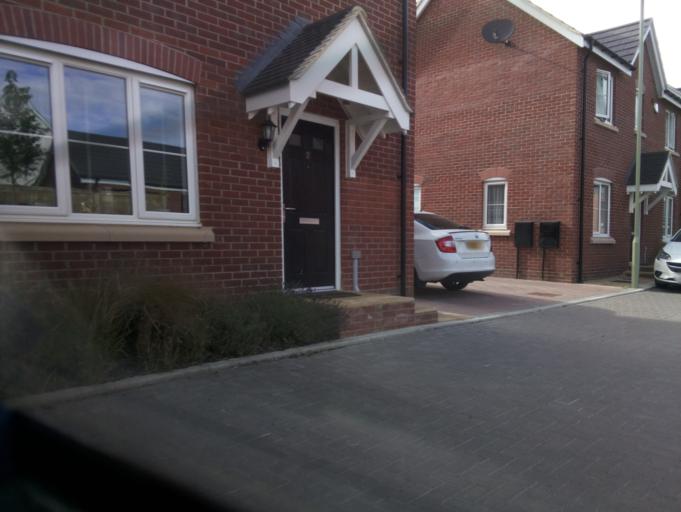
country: GB
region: England
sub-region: Gloucestershire
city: Stonehouse
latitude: 51.8067
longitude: -2.2696
